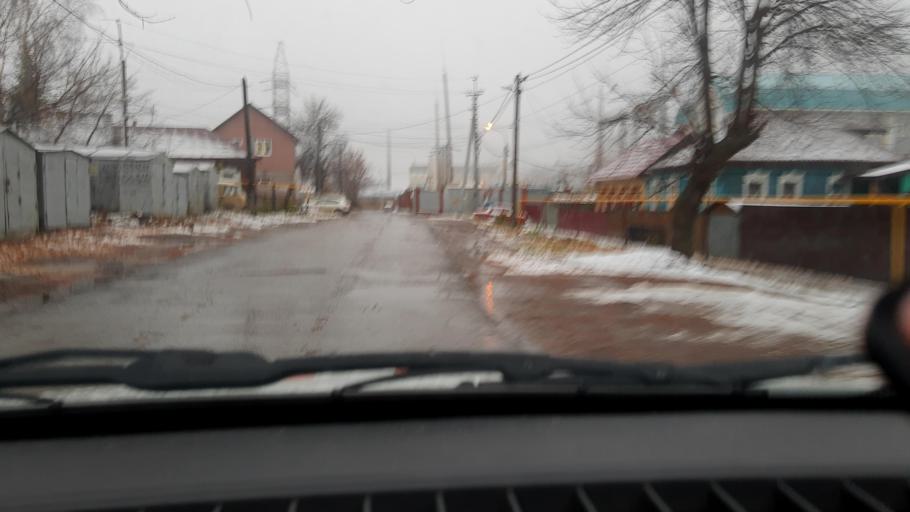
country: RU
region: Bashkortostan
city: Ufa
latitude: 54.7222
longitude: 55.9217
